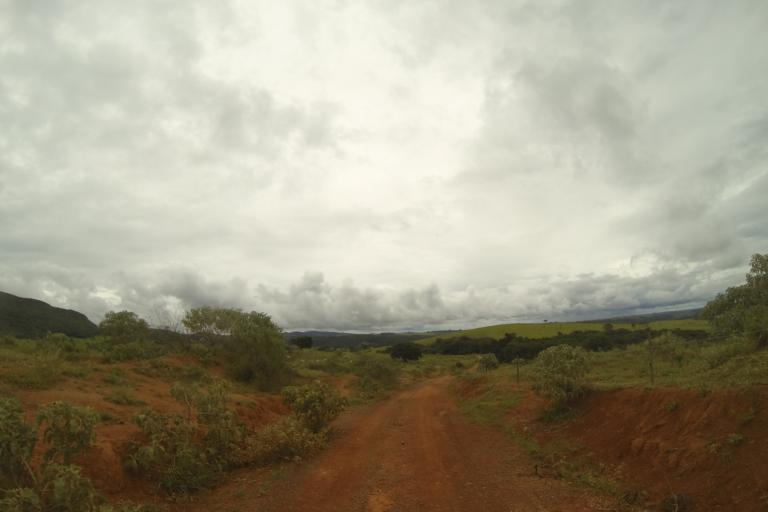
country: BR
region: Minas Gerais
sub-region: Ibia
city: Ibia
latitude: -19.7470
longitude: -46.5325
